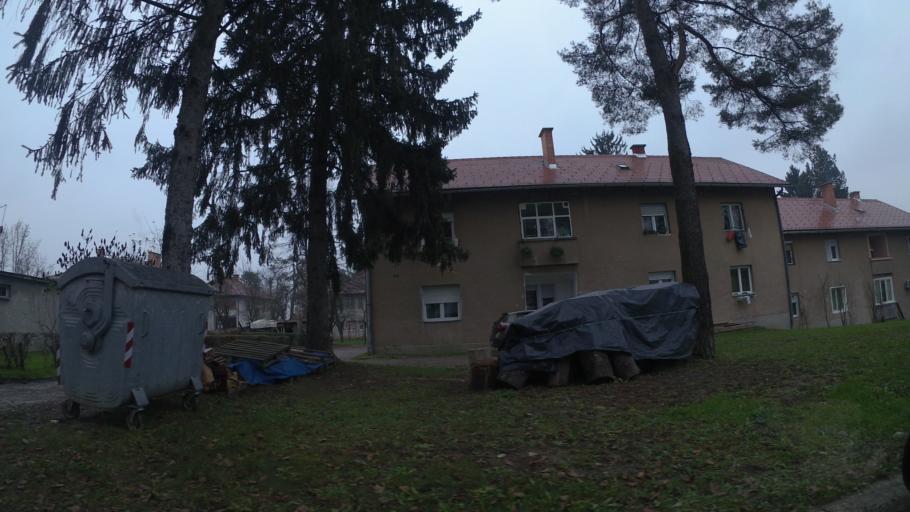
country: HR
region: Karlovacka
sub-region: Grad Karlovac
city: Karlovac
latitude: 45.4738
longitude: 15.5439
